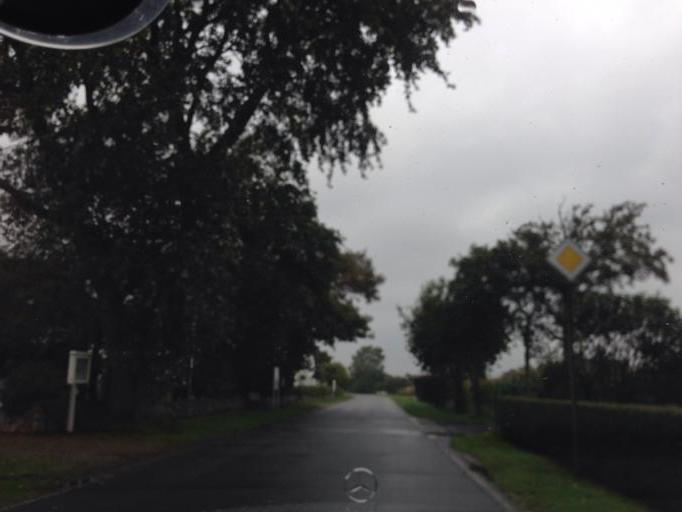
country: DE
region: Schleswig-Holstein
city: Dunsum
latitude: 54.7291
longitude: 8.4139
